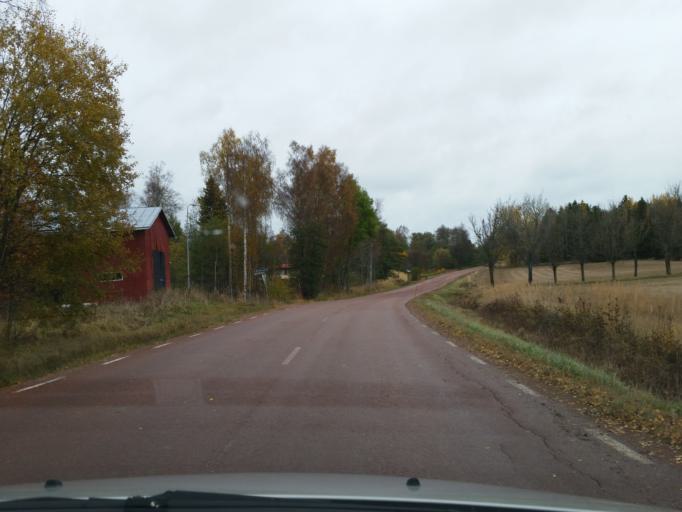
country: AX
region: Alands landsbygd
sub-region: Lemland
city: Lemland
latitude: 60.0630
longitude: 20.0981
